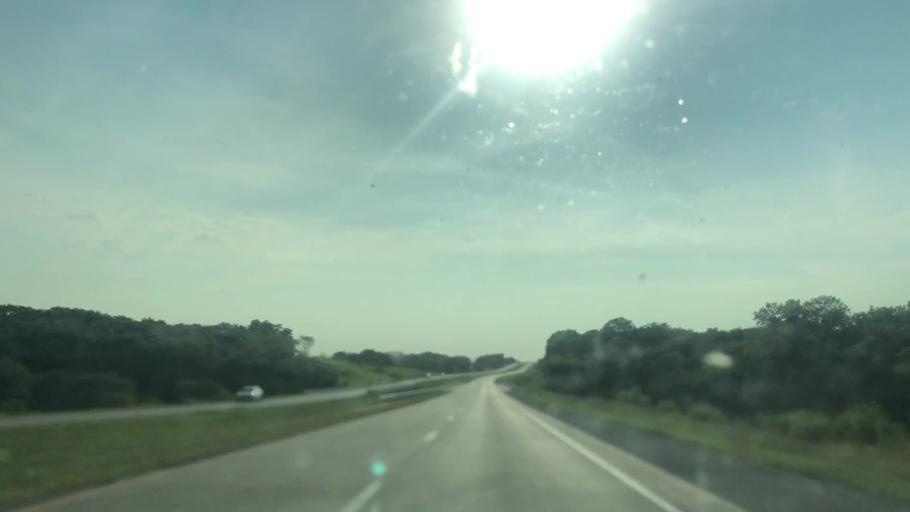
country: US
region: Iowa
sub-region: Story County
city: Nevada
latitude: 42.0078
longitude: -93.3733
